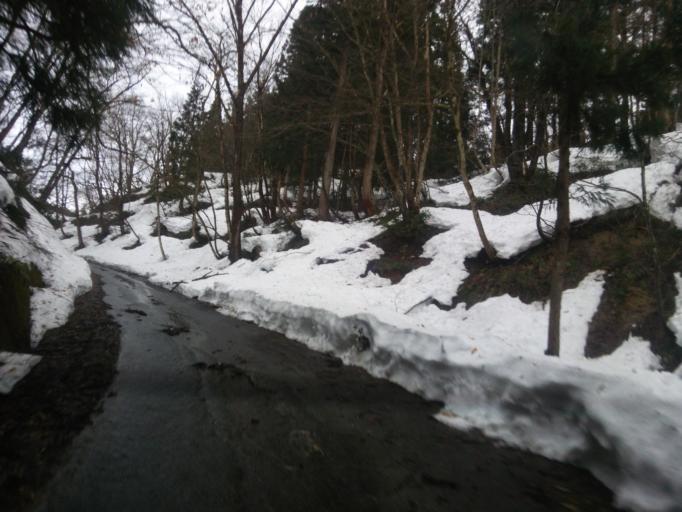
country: JP
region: Fukushima
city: Kitakata
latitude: 37.6888
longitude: 139.9442
